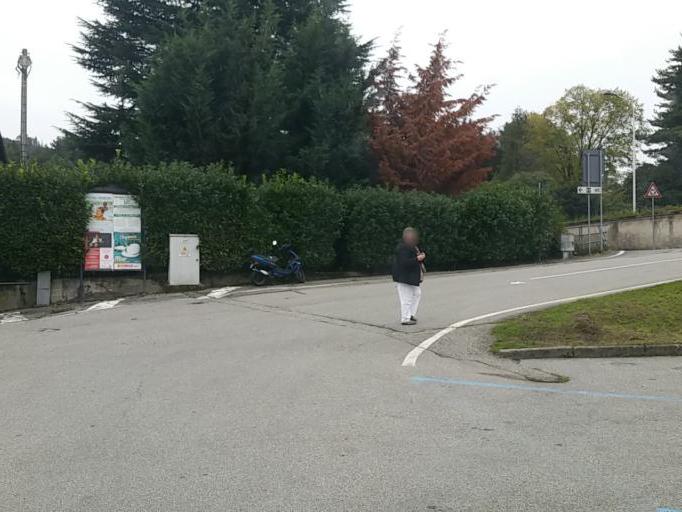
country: IT
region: Piedmont
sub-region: Provincia di Novara
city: Orta San Giulio
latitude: 45.7970
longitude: 8.4162
